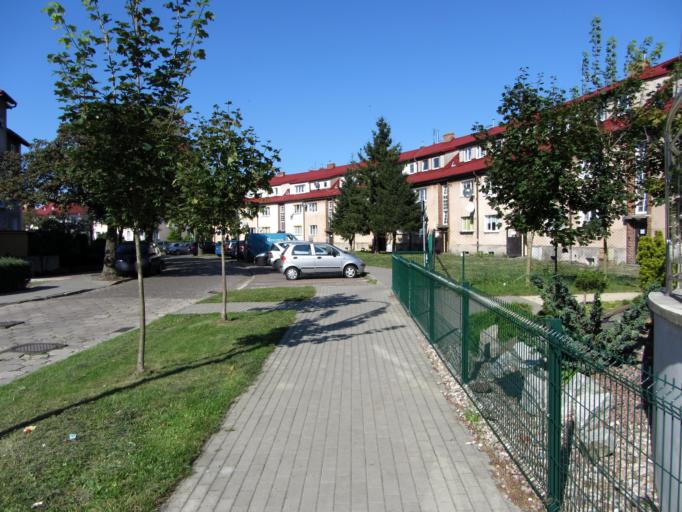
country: PL
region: West Pomeranian Voivodeship
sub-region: Powiat kolobrzeski
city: Kolobrzeg
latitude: 54.1692
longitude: 15.5687
